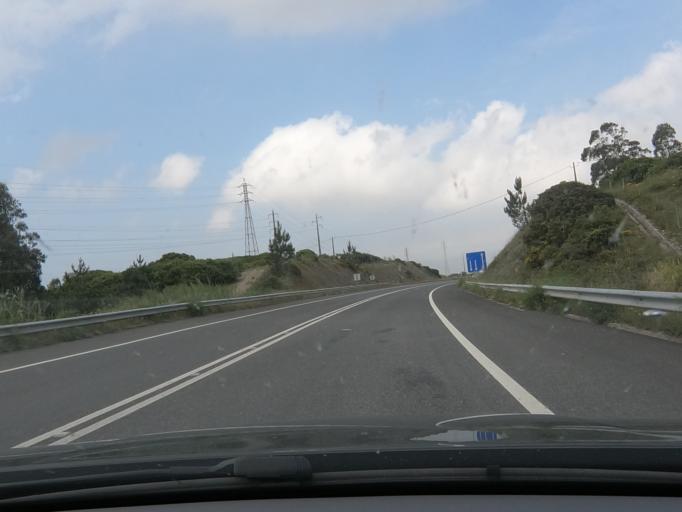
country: PT
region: Leiria
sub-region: Peniche
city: Atouguia da Baleia
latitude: 39.3238
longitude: -9.2747
